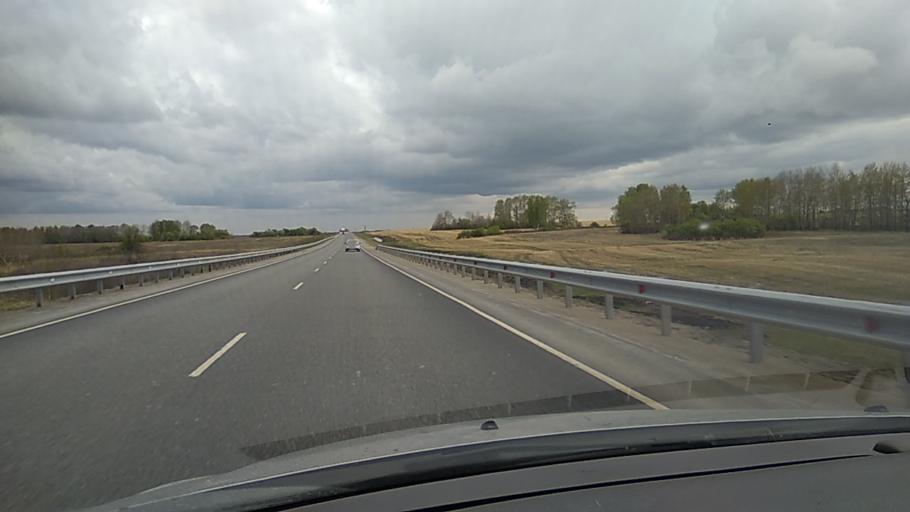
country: RU
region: Kurgan
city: Dalmatovo
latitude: 56.2885
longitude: 62.7619
